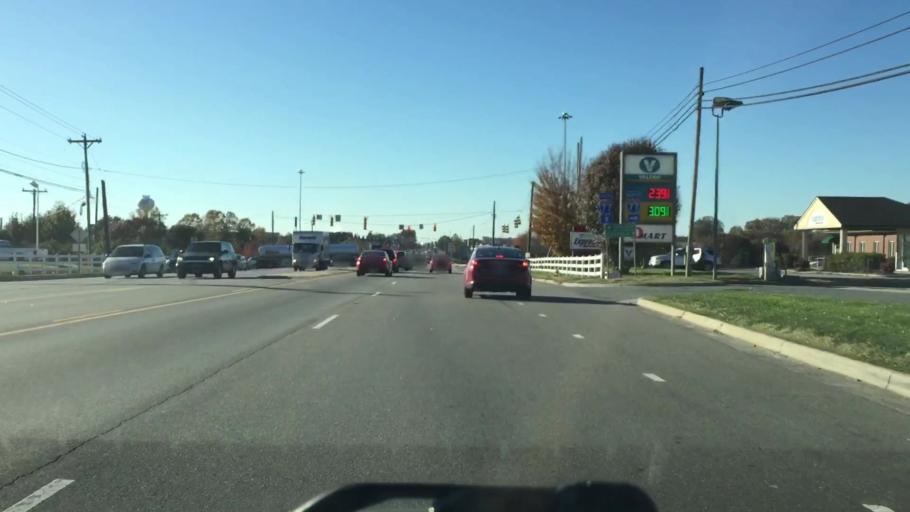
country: US
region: North Carolina
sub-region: Iredell County
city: Mooresville
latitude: 35.5937
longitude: -80.8576
